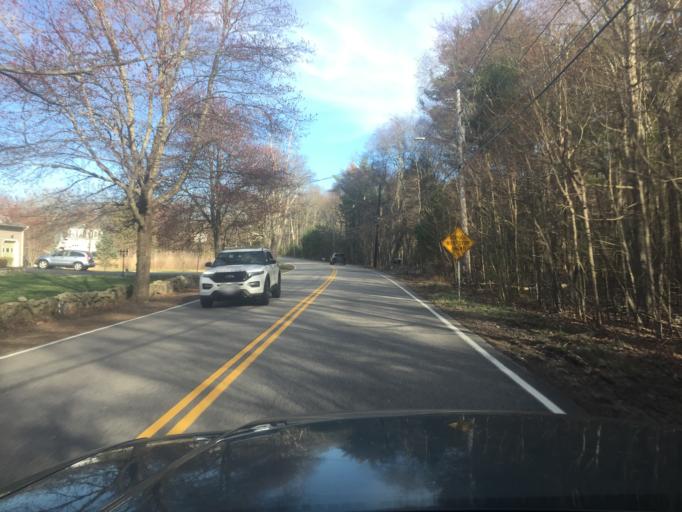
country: US
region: Massachusetts
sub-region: Worcester County
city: Milford
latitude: 42.1417
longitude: -71.4636
